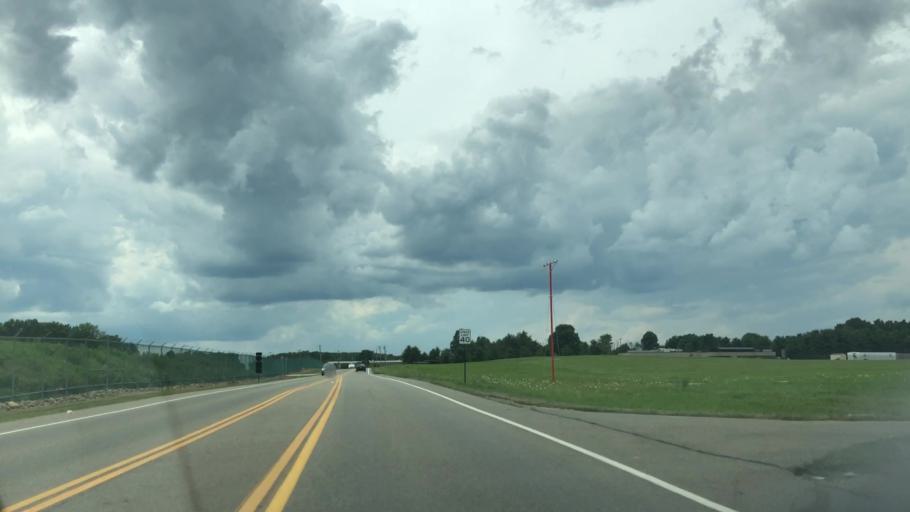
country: US
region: Ohio
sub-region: Summit County
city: Greensburg
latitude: 40.9294
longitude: -81.4393
